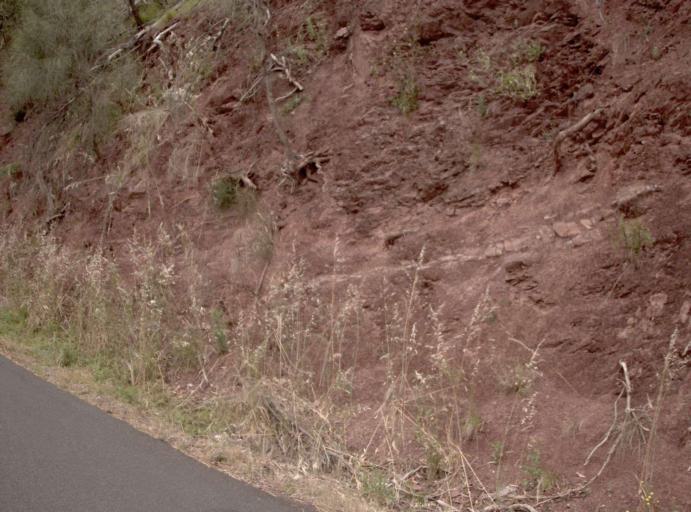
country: AU
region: Victoria
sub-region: Wellington
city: Heyfield
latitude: -37.7100
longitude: 146.6664
